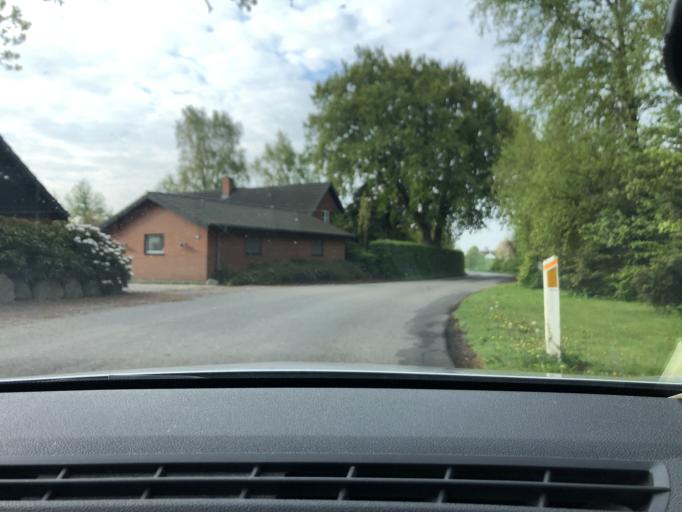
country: DK
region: Zealand
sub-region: Faxe Kommune
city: Ronnede
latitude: 55.2285
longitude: 12.0537
